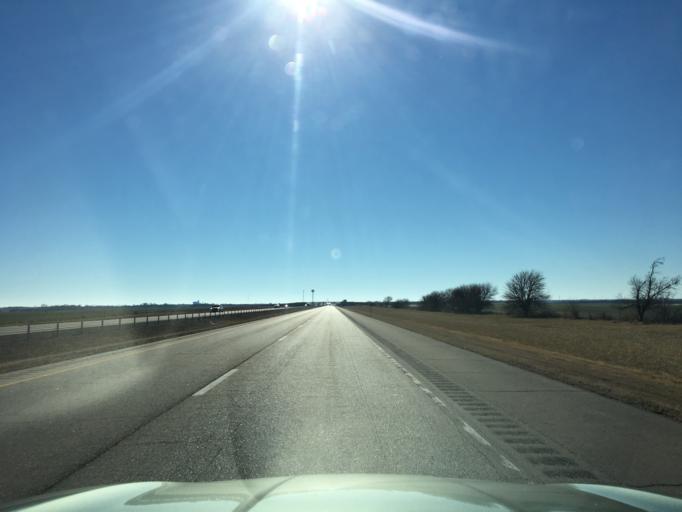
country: US
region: Oklahoma
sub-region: Kay County
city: Blackwell
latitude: 36.9639
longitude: -97.3458
